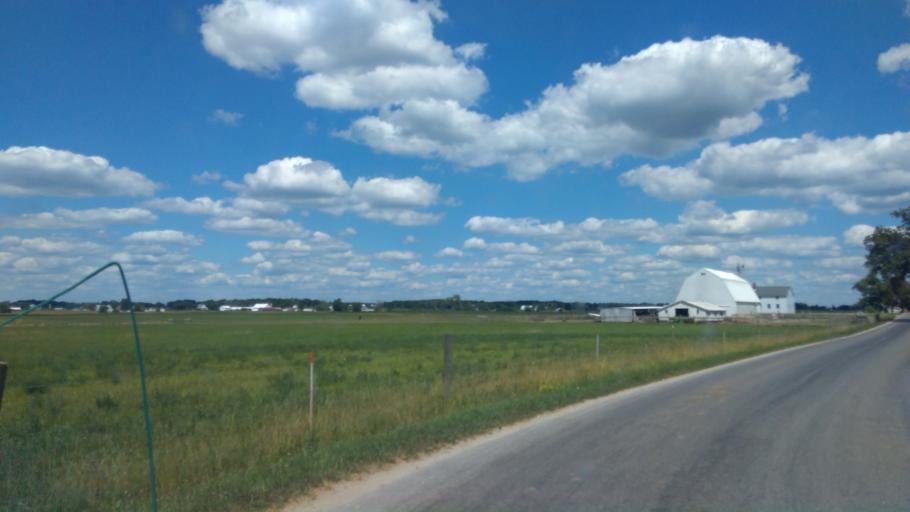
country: US
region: Indiana
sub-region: Adams County
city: Geneva
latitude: 40.5964
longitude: -84.9334
